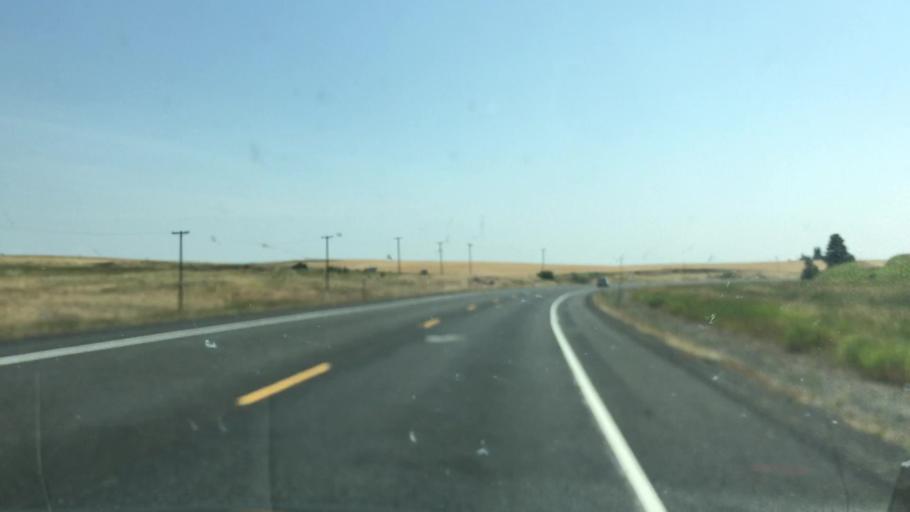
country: US
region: Idaho
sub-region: Lewis County
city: Nezperce
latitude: 46.2293
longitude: -116.4477
